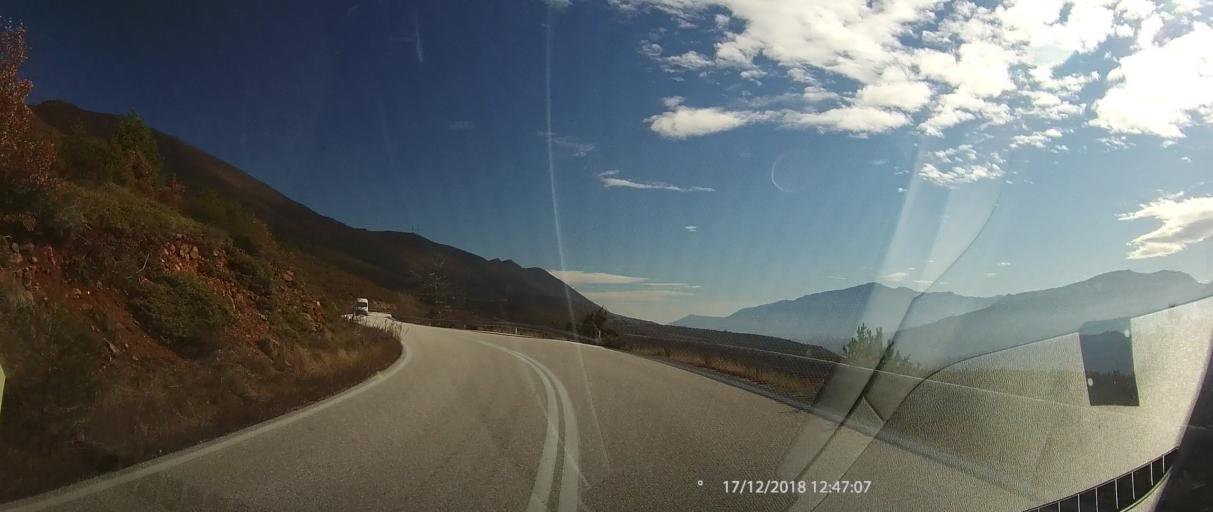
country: GR
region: Thessaly
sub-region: Trikala
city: Kastraki
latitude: 39.7858
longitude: 21.4237
